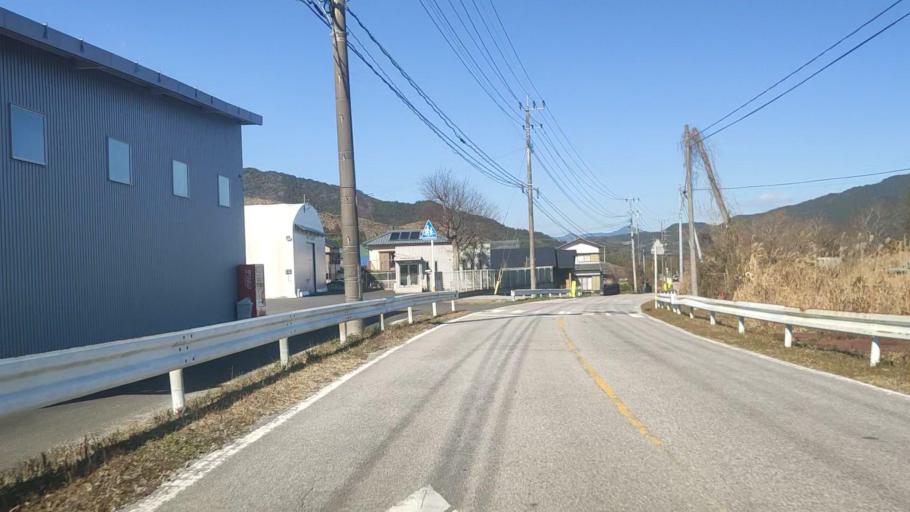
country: JP
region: Oita
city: Saiki
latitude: 32.9080
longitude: 131.9307
